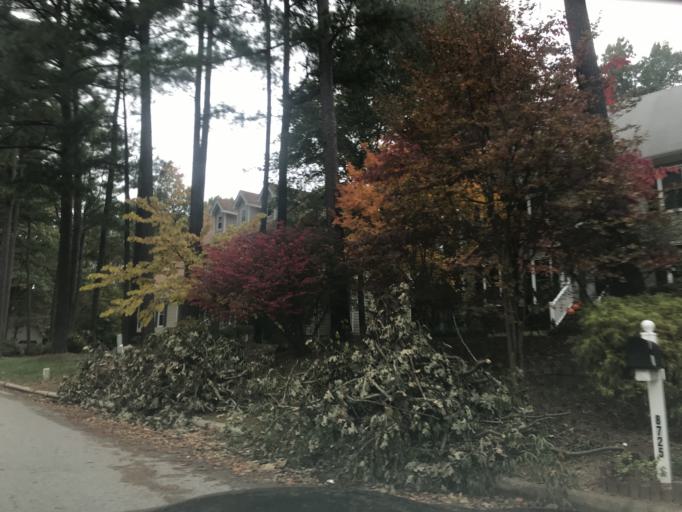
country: US
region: North Carolina
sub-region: Wake County
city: West Raleigh
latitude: 35.8905
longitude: -78.6306
